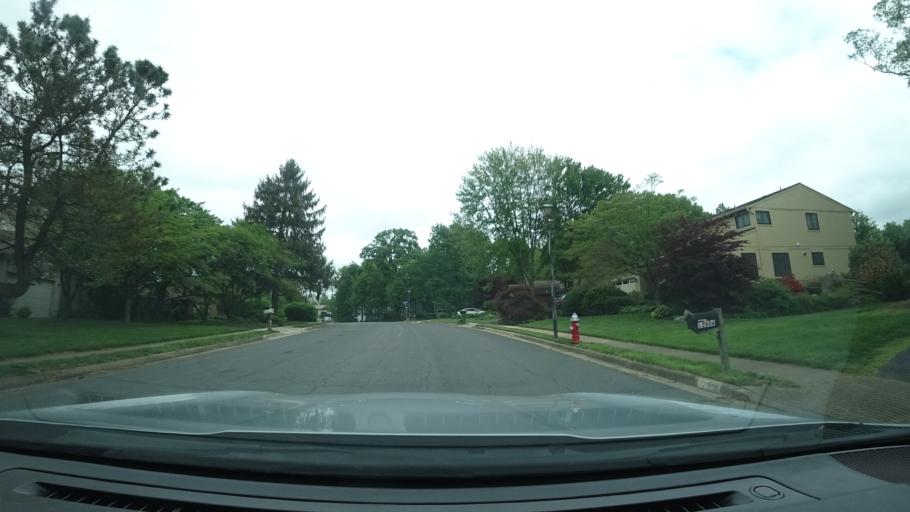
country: US
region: Virginia
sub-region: Fairfax County
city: Oak Hill
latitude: 38.9334
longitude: -77.3815
